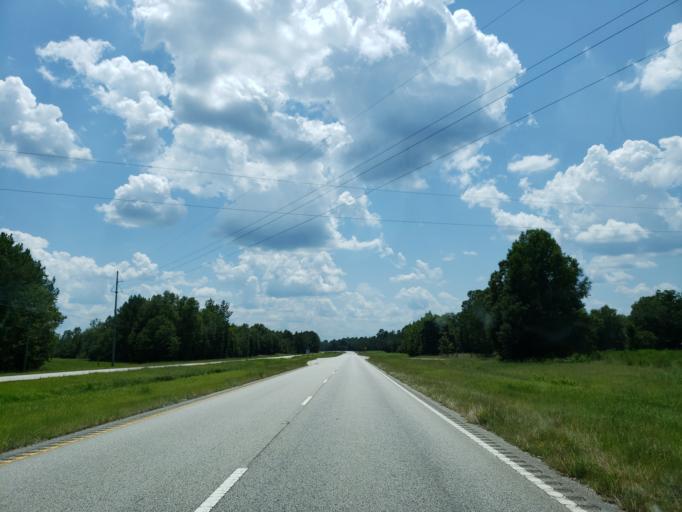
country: US
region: Mississippi
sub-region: Greene County
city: Leakesville
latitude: 31.2791
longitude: -88.5093
